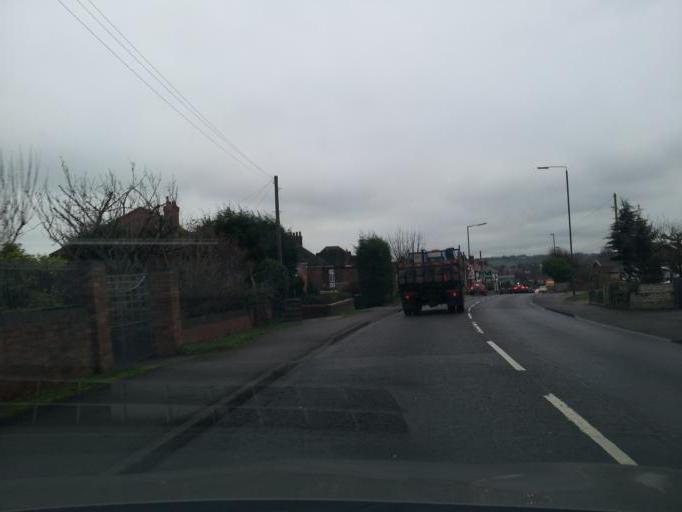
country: GB
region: England
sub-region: Derbyshire
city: Swadlincote
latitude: 52.7837
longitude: -1.5502
